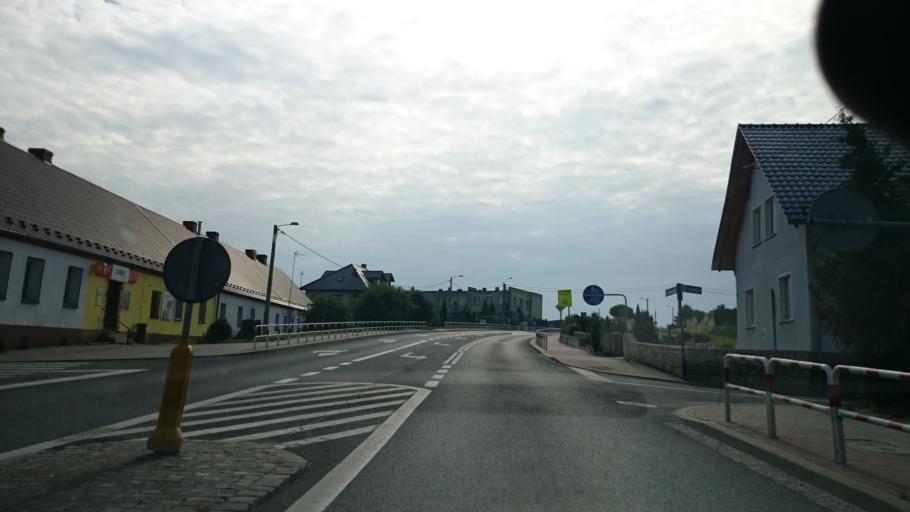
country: PL
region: Opole Voivodeship
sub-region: Powiat strzelecki
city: Jemielnica
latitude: 50.4888
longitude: 18.4114
